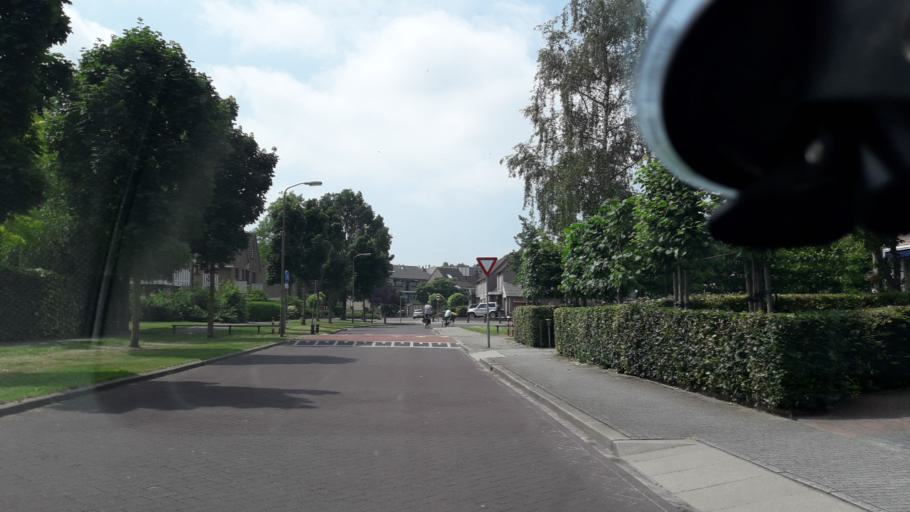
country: NL
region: Gelderland
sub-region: Gemeente Harderwijk
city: Harderwijk
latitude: 52.3455
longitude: 5.6482
